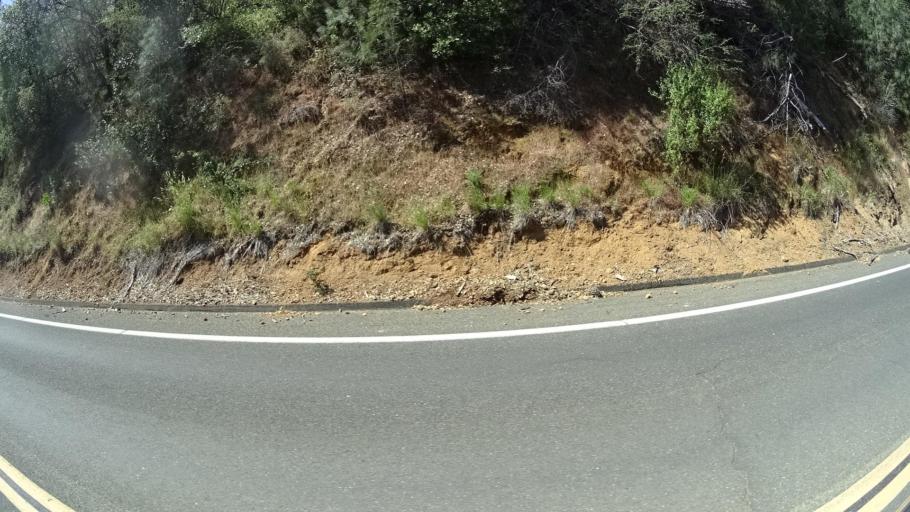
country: US
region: California
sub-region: Lake County
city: Clearlake
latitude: 38.9422
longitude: -122.6707
